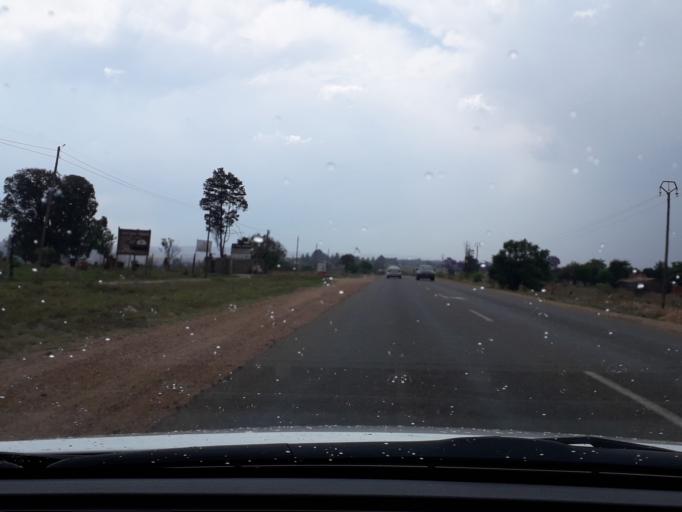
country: ZA
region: Gauteng
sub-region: West Rand District Municipality
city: Muldersdriseloop
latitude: -26.0115
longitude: 27.8586
